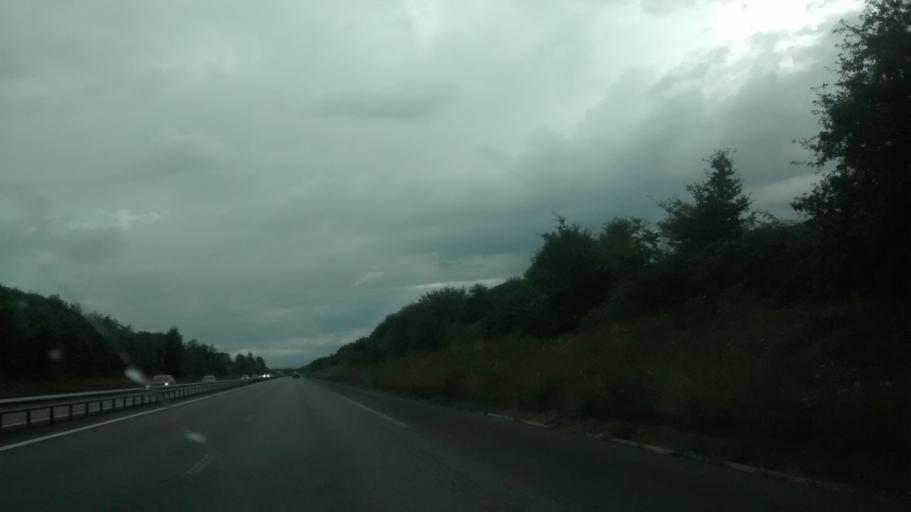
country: FR
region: Brittany
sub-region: Departement d'Ille-et-Vilaine
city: Saint-Jean-sur-Couesnon
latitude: 48.2912
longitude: -1.3757
